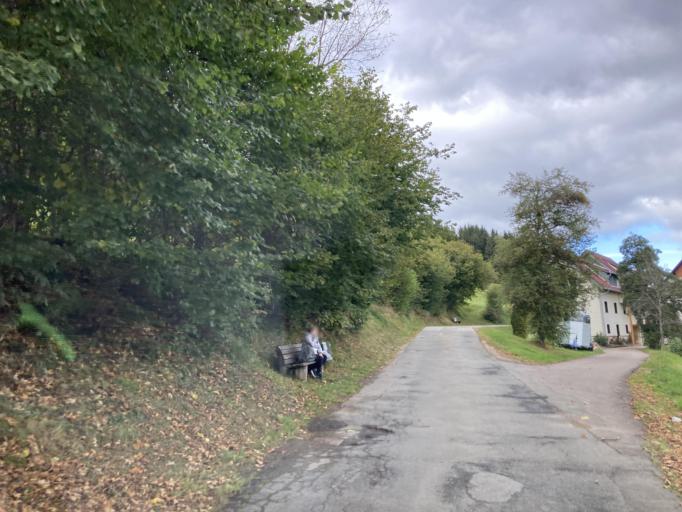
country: DE
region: Baden-Wuerttemberg
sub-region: Freiburg Region
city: Vohrenbach
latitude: 48.0490
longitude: 8.3023
